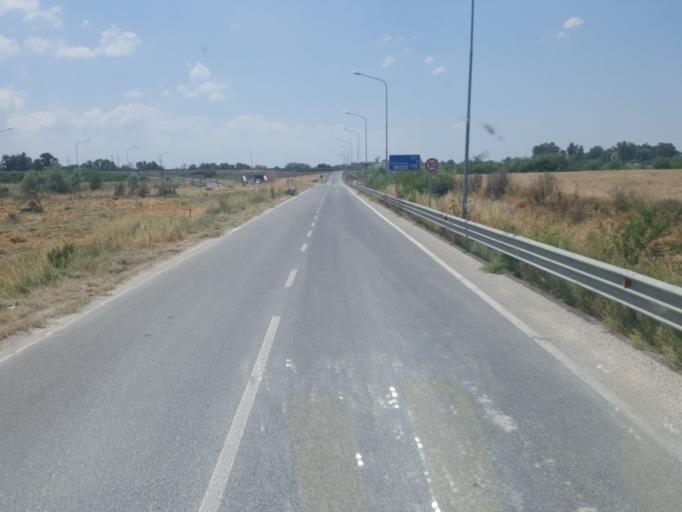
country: IT
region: Latium
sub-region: Citta metropolitana di Roma Capitale
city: Fiano Romano
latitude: 42.1570
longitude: 12.6430
